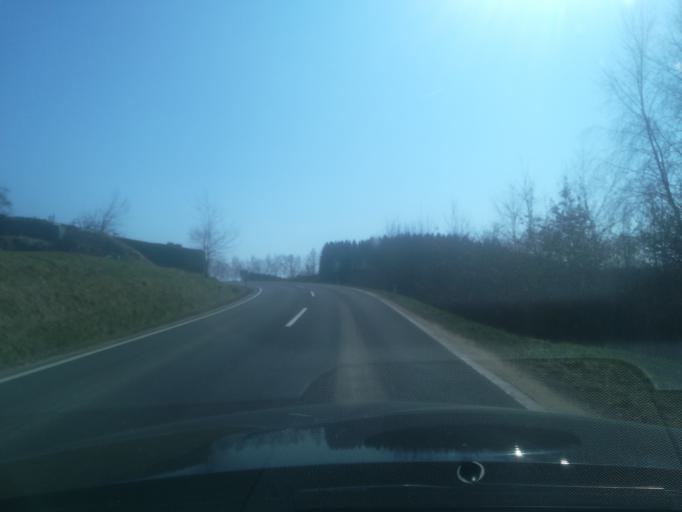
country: AT
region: Upper Austria
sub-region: Politischer Bezirk Freistadt
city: Freistadt
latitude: 48.4210
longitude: 14.6049
